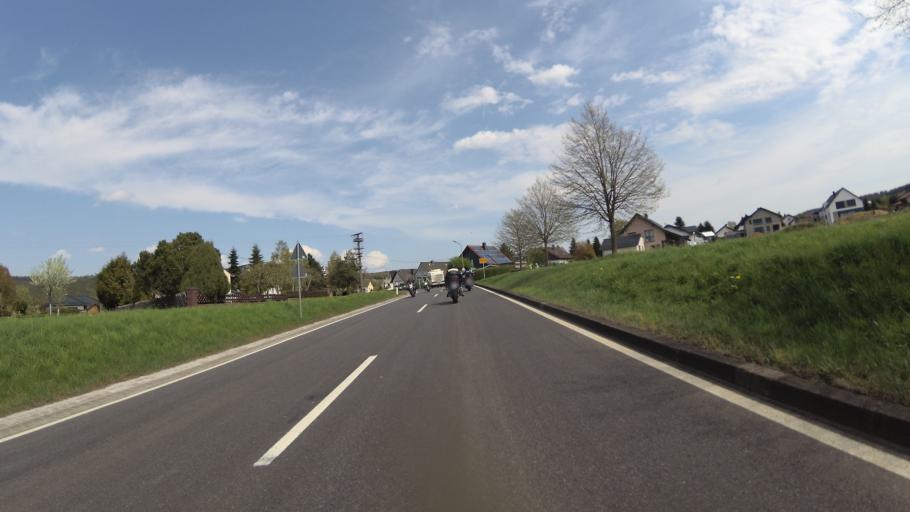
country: DE
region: Rheinland-Pfalz
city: Mullenbach
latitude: 50.3172
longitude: 6.9084
